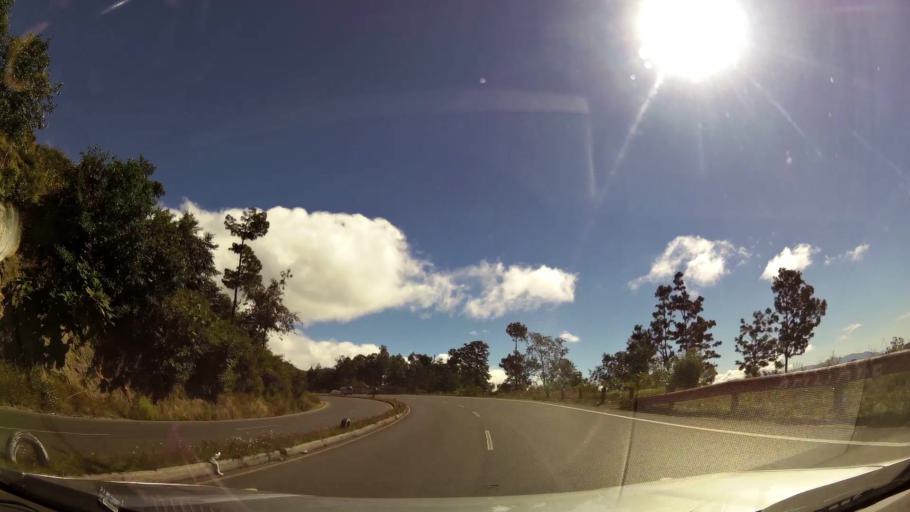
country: GT
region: Solola
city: Solola
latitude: 14.8274
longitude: -91.1853
